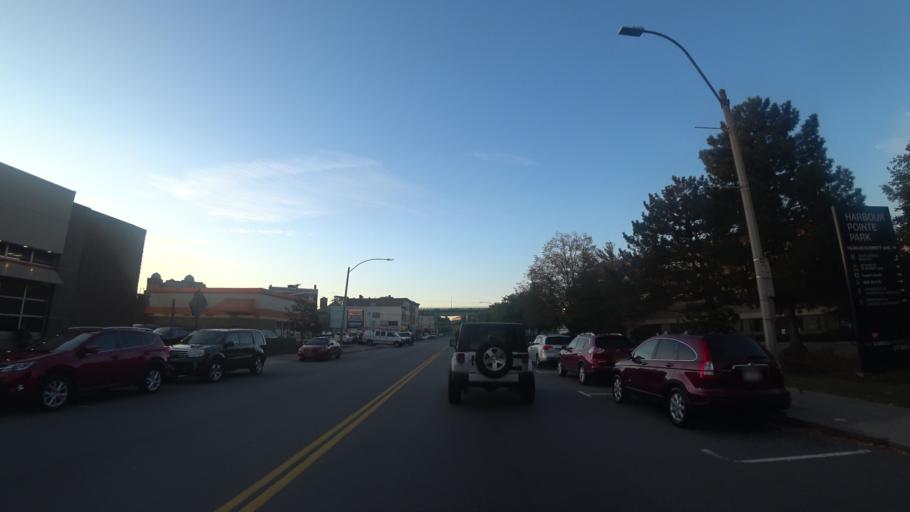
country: US
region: Massachusetts
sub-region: Suffolk County
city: Chelsea
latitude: 42.3942
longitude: -71.0393
